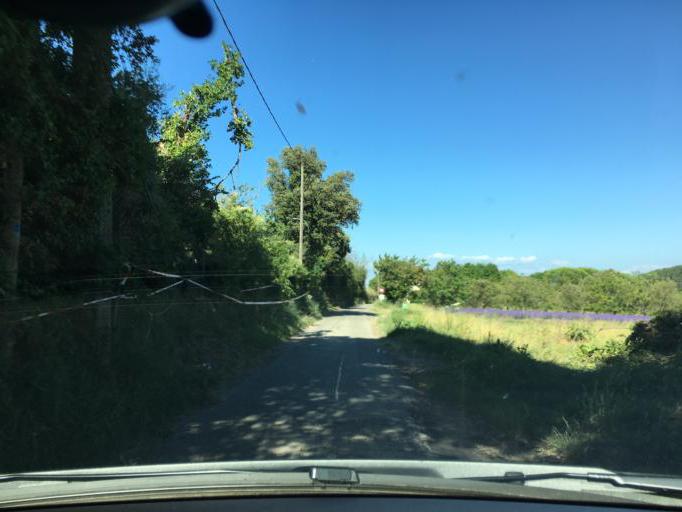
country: FR
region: Provence-Alpes-Cote d'Azur
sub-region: Departement du Vaucluse
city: Bollene
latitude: 44.3075
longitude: 4.7736
